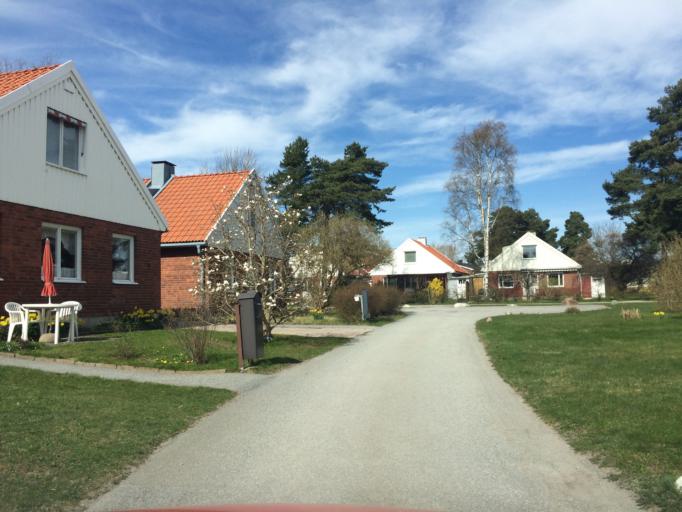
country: SE
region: Stockholm
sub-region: Huddinge Kommun
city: Segeltorp
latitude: 59.2869
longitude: 17.9759
